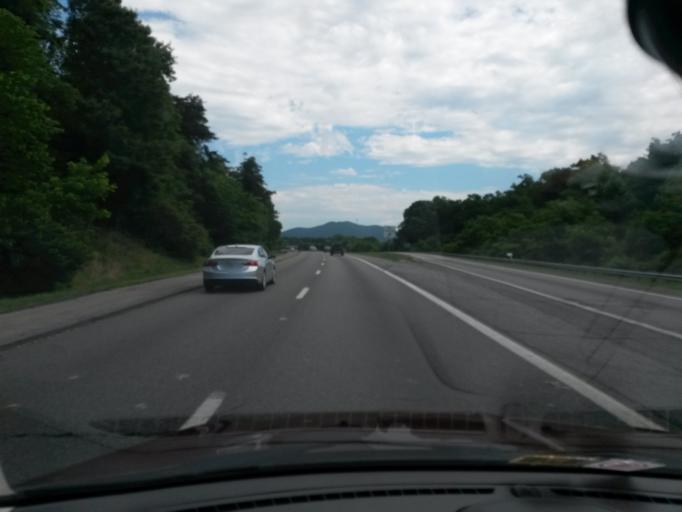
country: US
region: Virginia
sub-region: Botetourt County
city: Cloverdale
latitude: 37.3670
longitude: -79.9230
